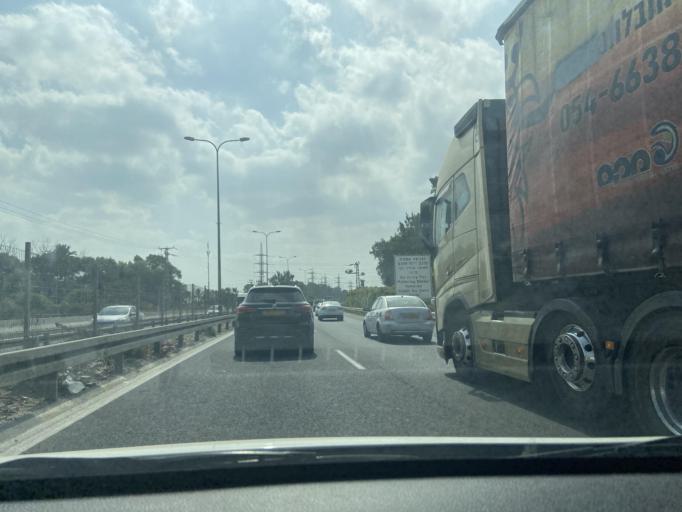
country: IL
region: Northern District
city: `Akko
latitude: 32.8985
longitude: 35.0927
